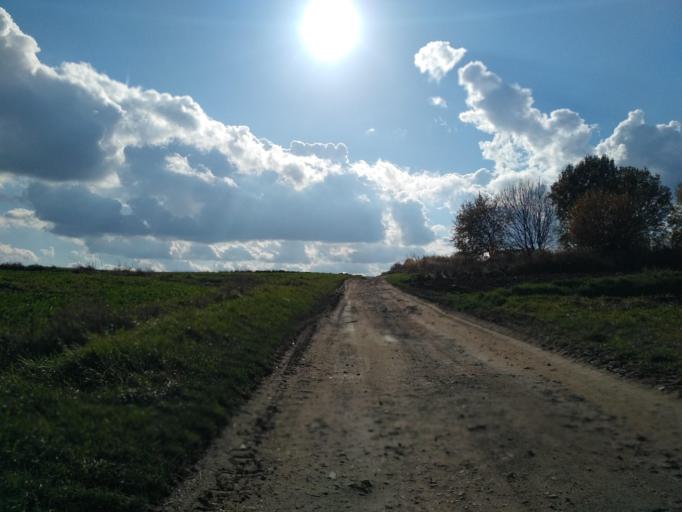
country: PL
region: Subcarpathian Voivodeship
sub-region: Powiat rzeszowski
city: Zglobien
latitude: 50.0039
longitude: 21.8628
